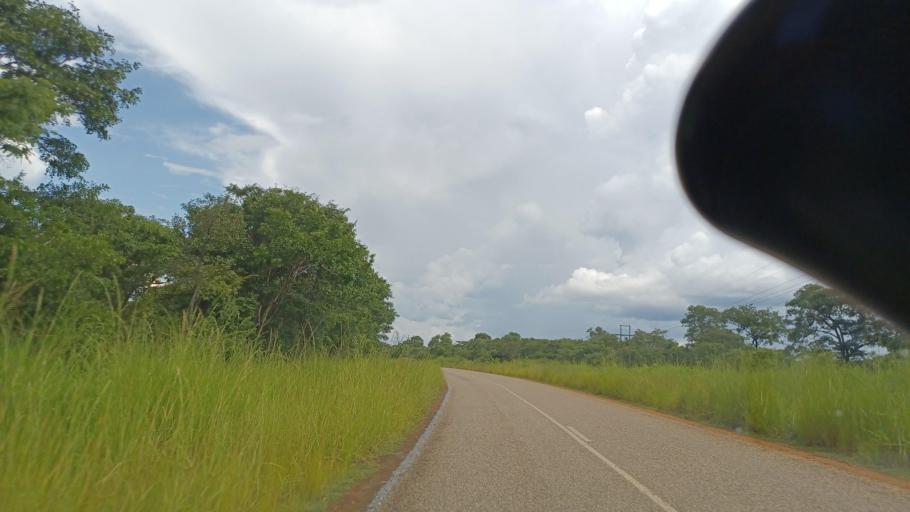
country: ZM
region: North-Western
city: Kasempa
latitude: -13.1530
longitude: 25.8776
